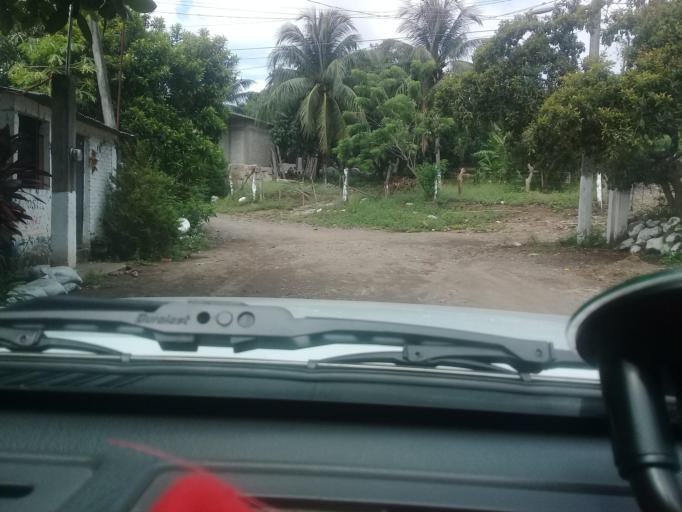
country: MX
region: Veracruz
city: Paso de Ovejas
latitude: 19.2921
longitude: -96.4357
